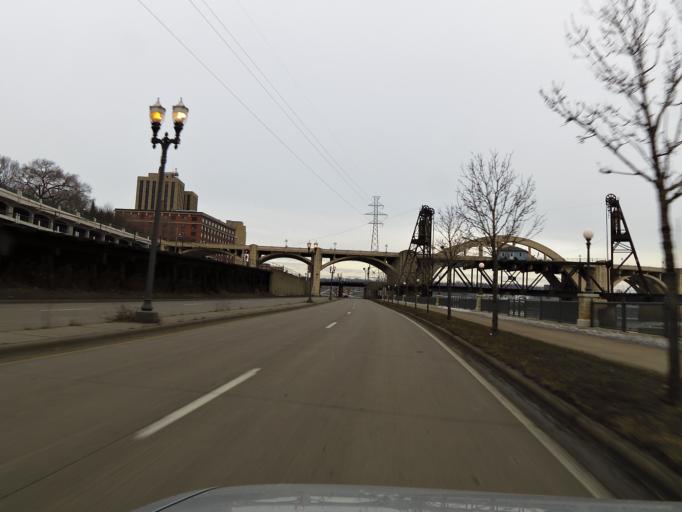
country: US
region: Minnesota
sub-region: Ramsey County
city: Saint Paul
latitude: 44.9438
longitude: -93.0904
